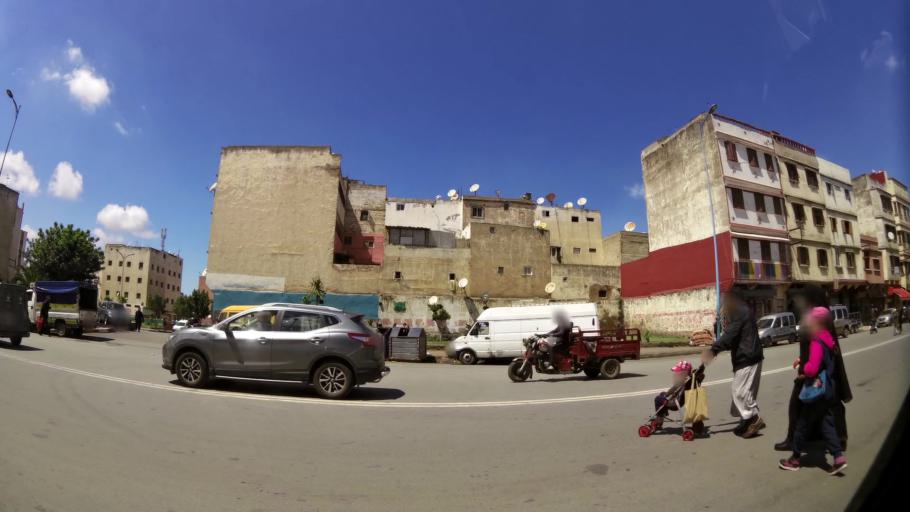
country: MA
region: Grand Casablanca
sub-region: Casablanca
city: Casablanca
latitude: 33.5656
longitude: -7.5858
